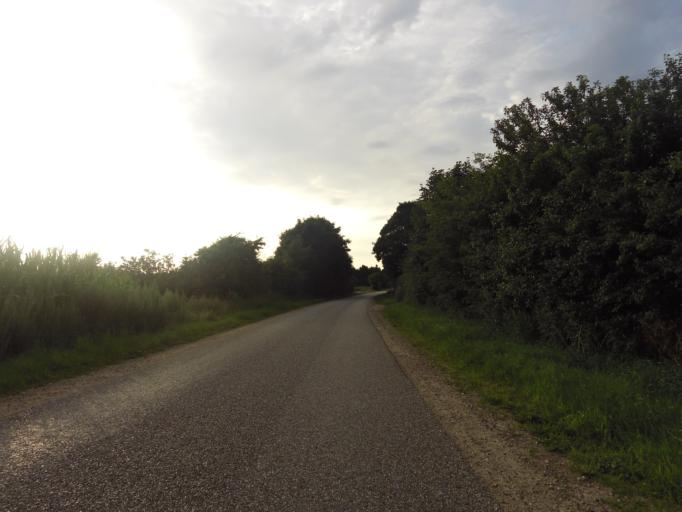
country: DK
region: South Denmark
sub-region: Tonder Kommune
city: Logumkloster
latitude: 55.1572
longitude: 8.9331
